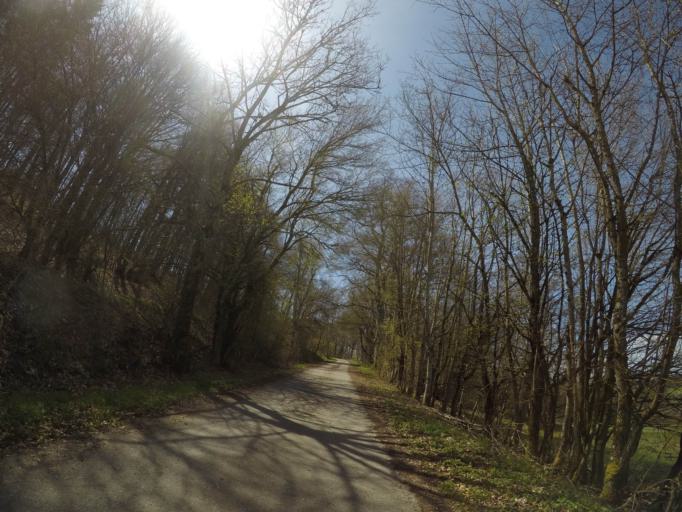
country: DE
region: Baden-Wuerttemberg
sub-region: Regierungsbezirk Stuttgart
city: Neidlingen
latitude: 48.5287
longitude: 9.5668
